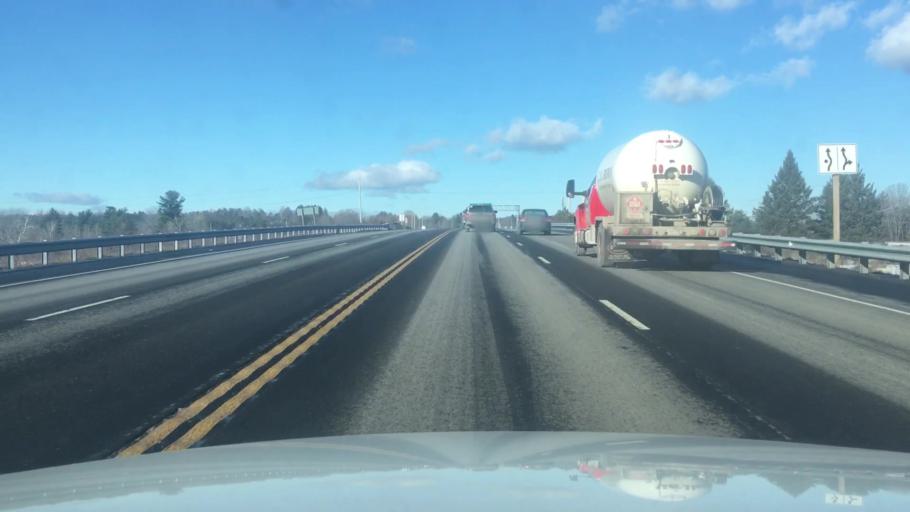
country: US
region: Maine
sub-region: Kennebec County
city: Augusta
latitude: 44.3510
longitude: -69.7768
